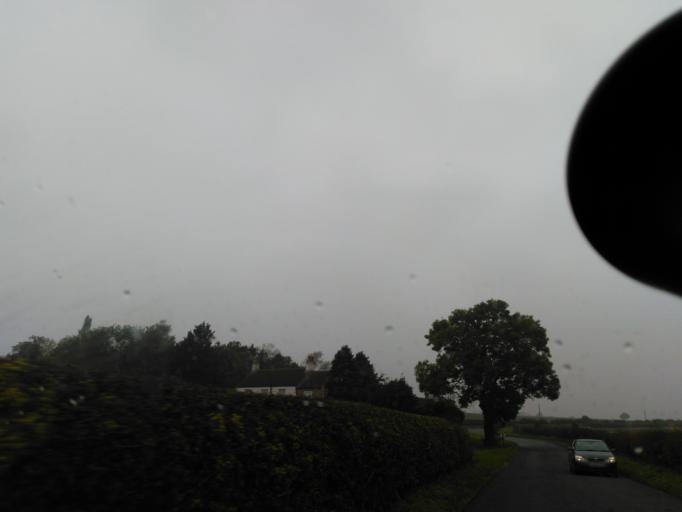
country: GB
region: England
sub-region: North Yorkshire
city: Bedale
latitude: 54.3136
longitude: -1.5635
